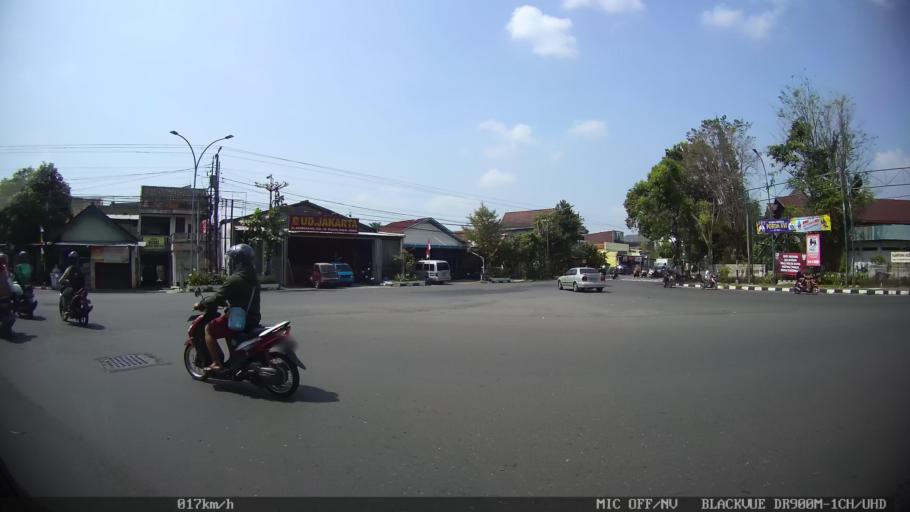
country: ID
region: Daerah Istimewa Yogyakarta
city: Yogyakarta
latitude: -7.8144
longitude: 110.3915
